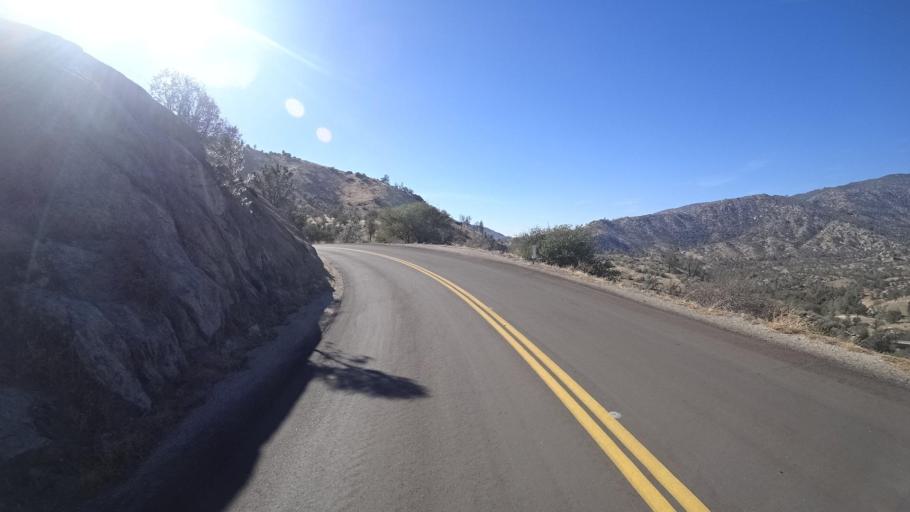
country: US
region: California
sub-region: Kern County
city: Bodfish
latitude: 35.5944
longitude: -118.5153
